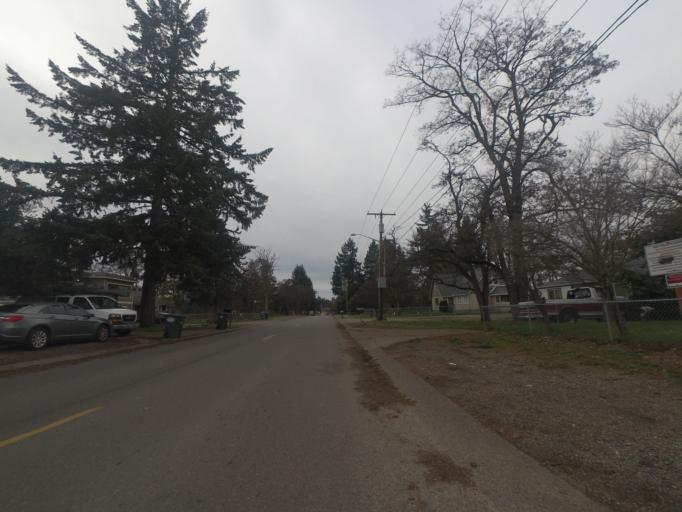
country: US
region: Washington
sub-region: Pierce County
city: McChord Air Force Base
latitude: 47.1249
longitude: -122.5311
